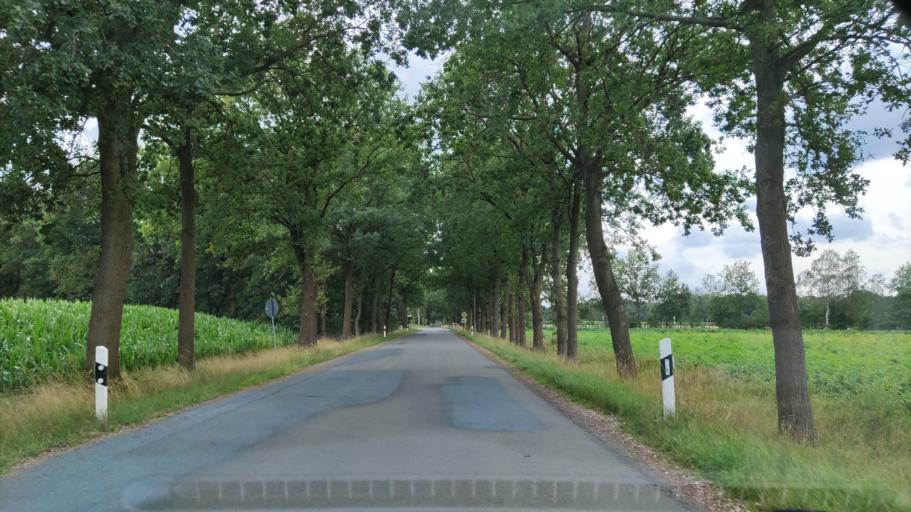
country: DE
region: Lower Saxony
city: Dannenberg
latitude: 53.0752
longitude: 11.1279
